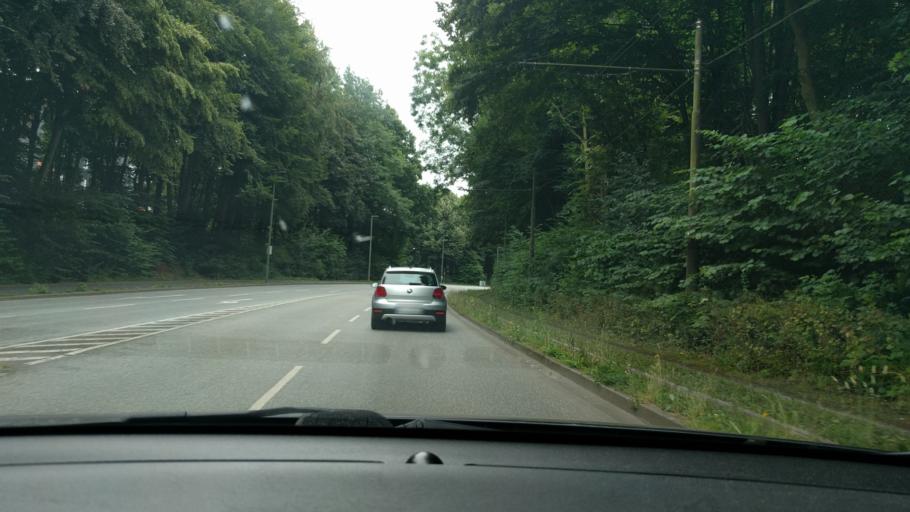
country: DE
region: North Rhine-Westphalia
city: Witten
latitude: 51.4628
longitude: 7.3000
